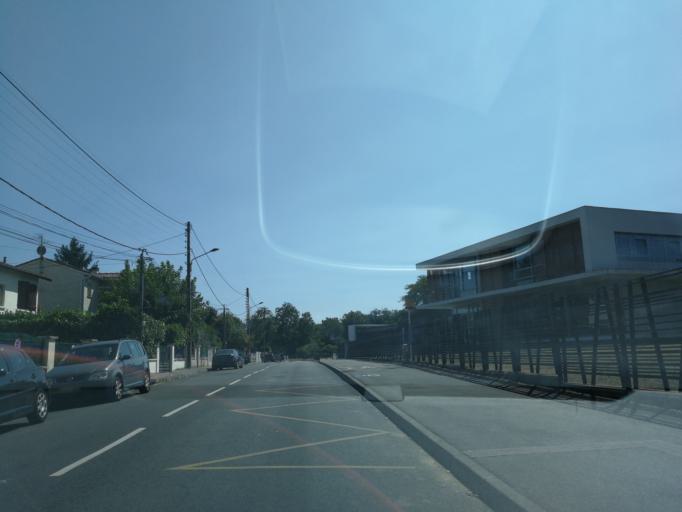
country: FR
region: Midi-Pyrenees
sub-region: Departement de la Haute-Garonne
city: Balma
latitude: 43.5941
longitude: 1.4881
